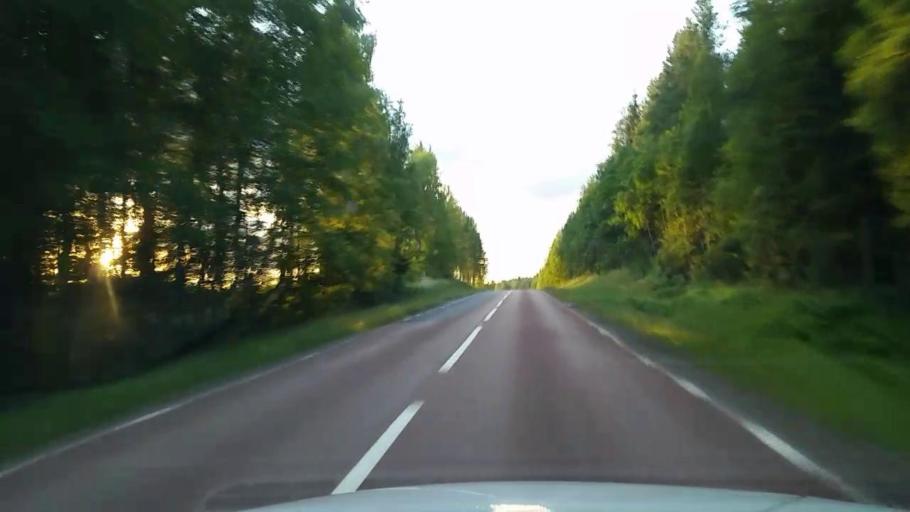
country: SE
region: Gaevleborg
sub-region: Ljusdals Kommun
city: Farila
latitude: 62.1451
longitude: 15.6856
